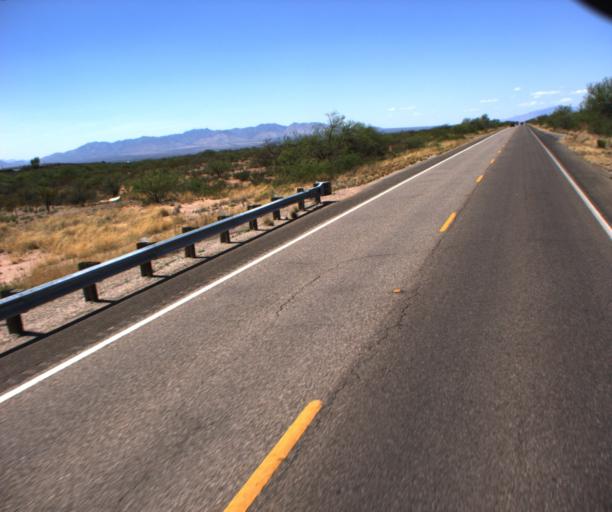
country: US
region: Arizona
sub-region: Cochise County
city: Tombstone
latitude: 31.7548
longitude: -110.1045
